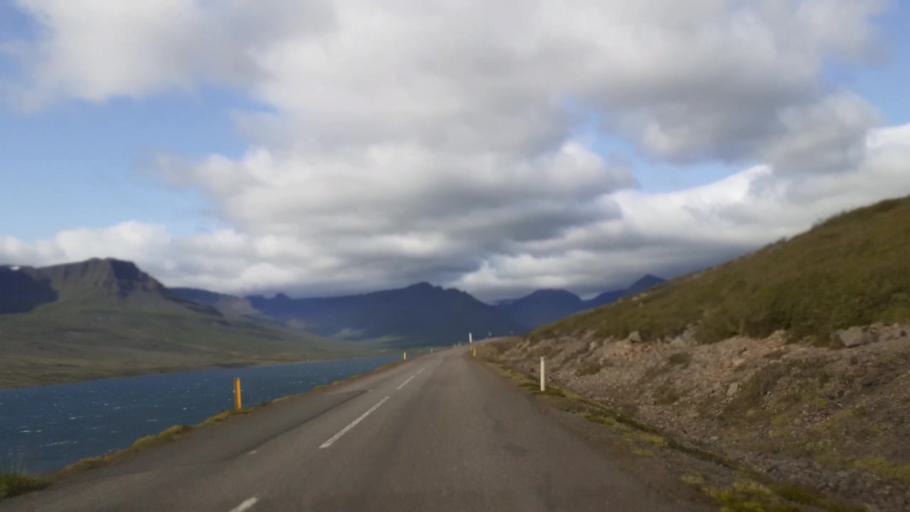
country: IS
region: East
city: Eskifjoerdur
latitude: 64.9223
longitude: -13.9706
